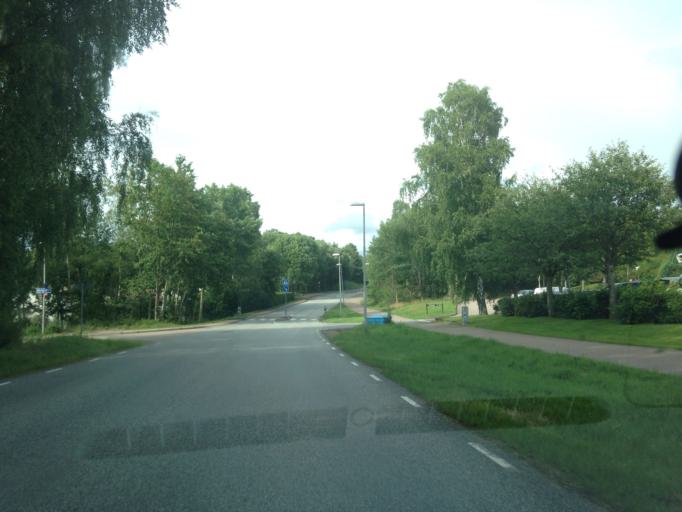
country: SE
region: Vaestra Goetaland
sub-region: Goteborg
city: Goeteborg
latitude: 57.7600
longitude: 11.9661
